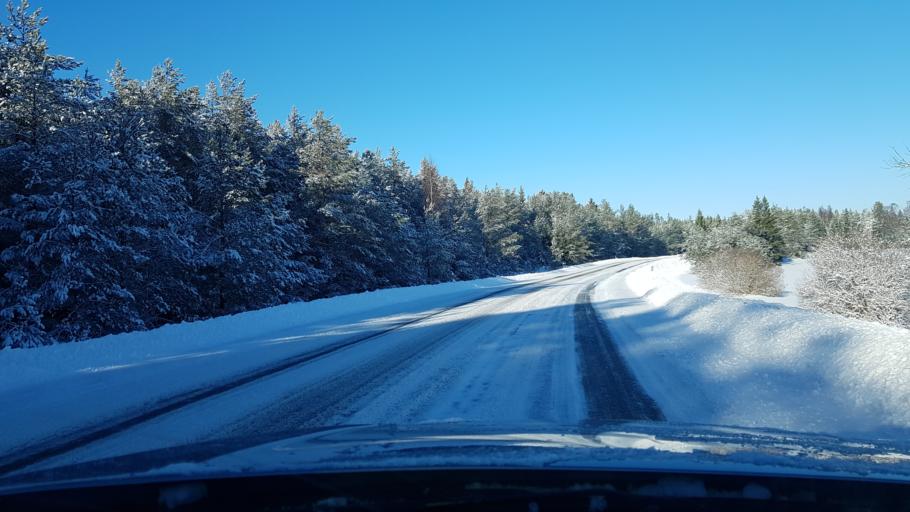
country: EE
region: Hiiumaa
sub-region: Kaerdla linn
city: Kardla
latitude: 58.9470
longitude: 22.7717
